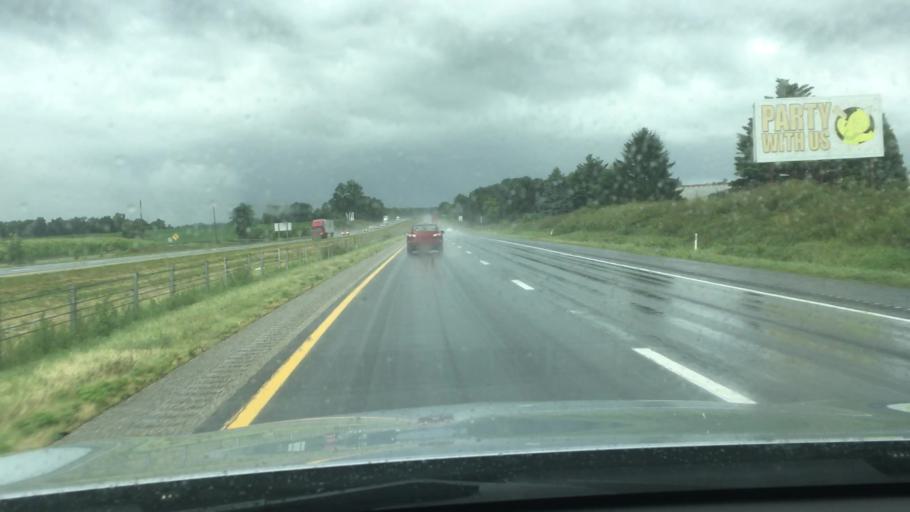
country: US
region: Pennsylvania
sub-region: Cumberland County
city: Shippensburg
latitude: 40.0642
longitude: -77.4749
